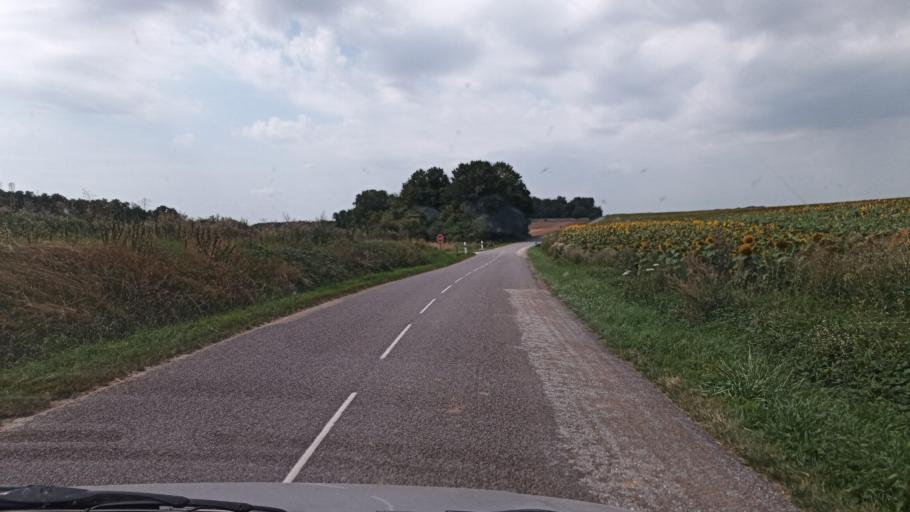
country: FR
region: Bourgogne
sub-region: Departement de l'Yonne
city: Egriselles-le-Bocage
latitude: 48.0350
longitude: 3.1932
